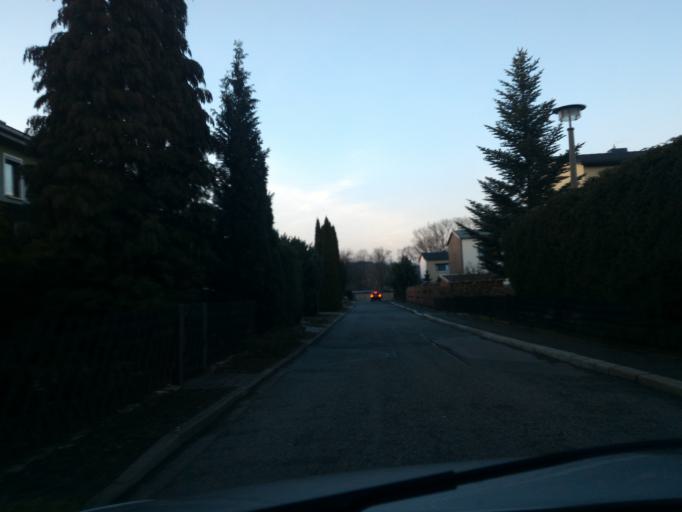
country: DE
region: Saxony
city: Grossschonau
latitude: 50.8905
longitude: 14.6664
